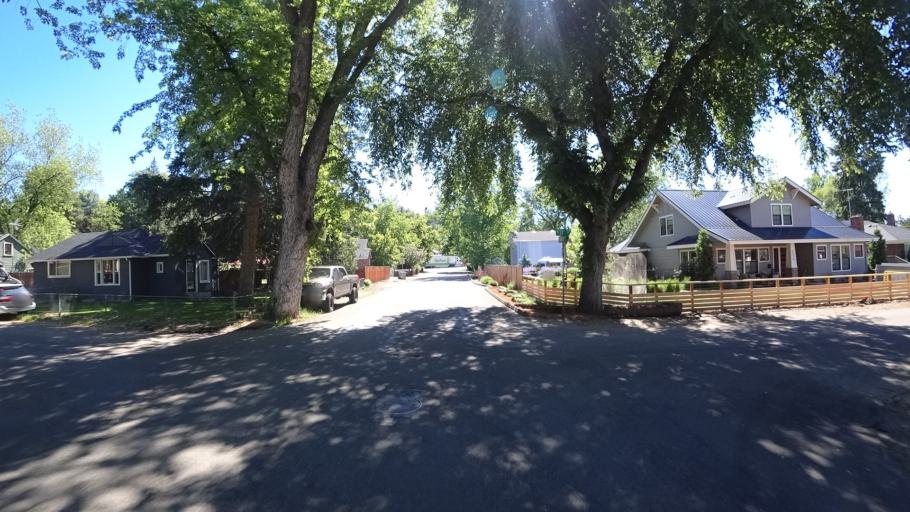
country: US
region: Idaho
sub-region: Ada County
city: Garden City
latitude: 43.6425
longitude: -116.2147
